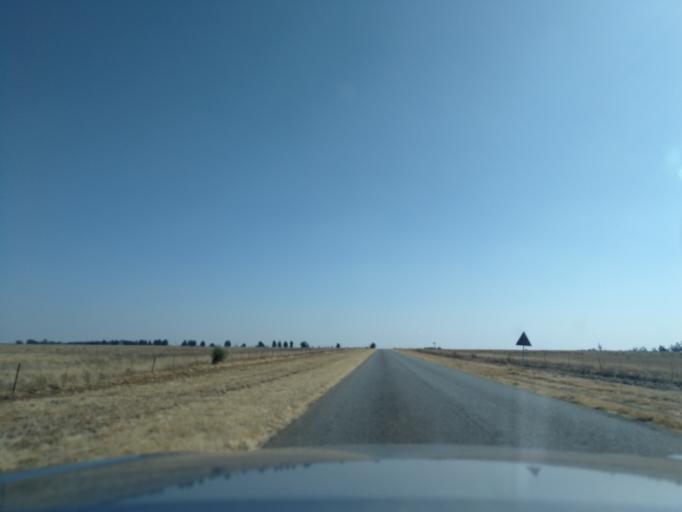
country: ZA
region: Orange Free State
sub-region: Fezile Dabi District Municipality
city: Viljoenskroon
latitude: -27.0675
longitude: 26.8360
